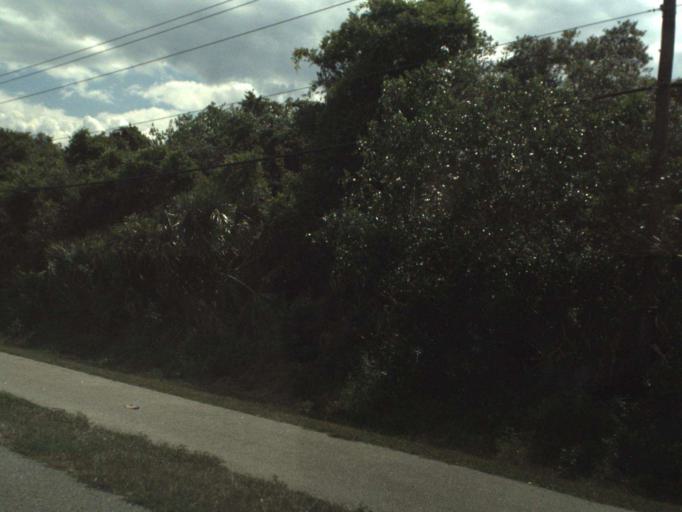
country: US
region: Florida
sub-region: Brevard County
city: Titusville
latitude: 28.5911
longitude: -80.8470
